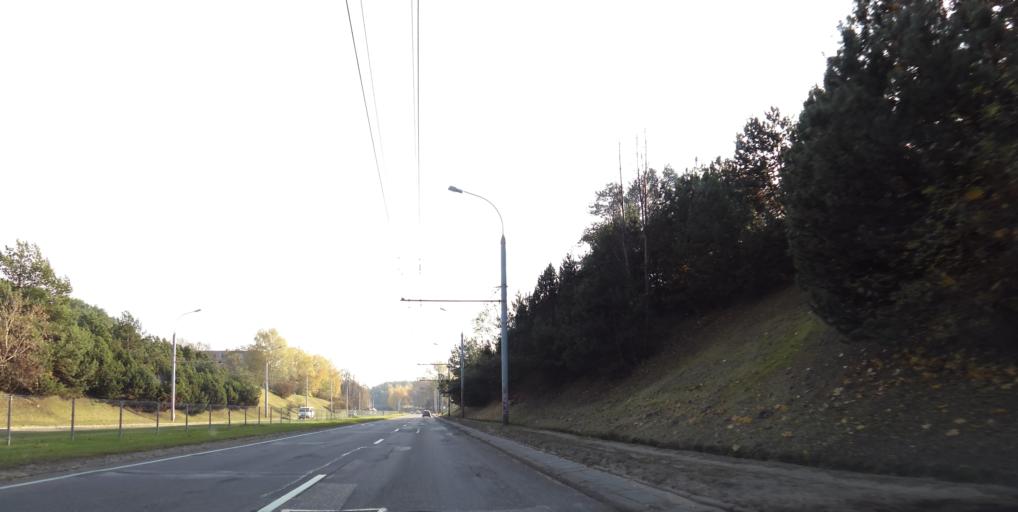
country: LT
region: Vilnius County
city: Lazdynai
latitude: 54.6803
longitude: 25.2099
